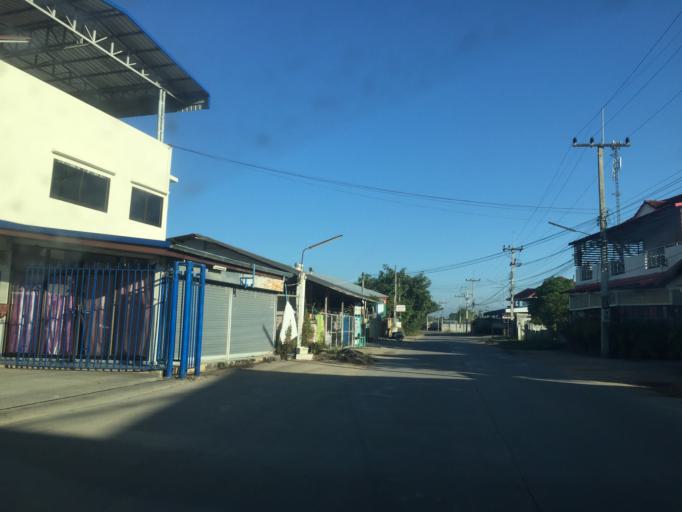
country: TH
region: Lamphun
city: Lamphun
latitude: 18.6110
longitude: 99.0564
